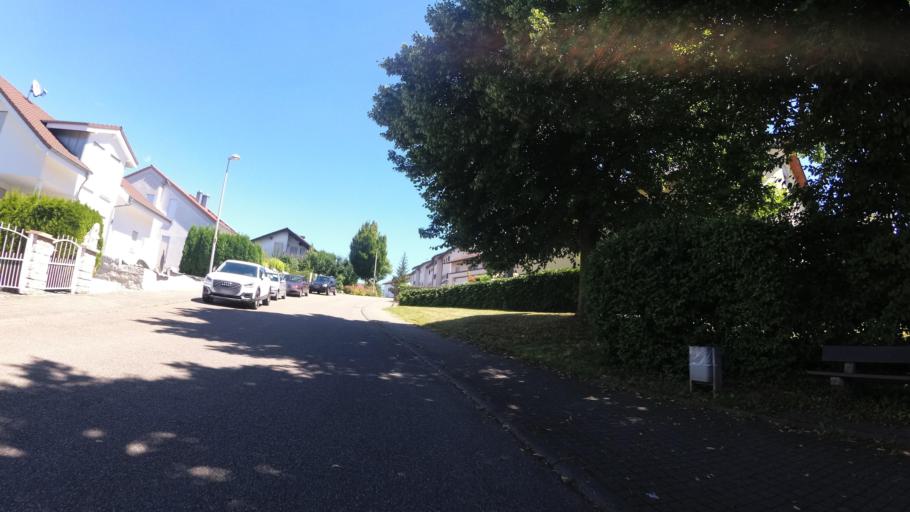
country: DE
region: Baden-Wuerttemberg
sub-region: Regierungsbezirk Stuttgart
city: Nordheim
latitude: 49.1193
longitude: 9.1504
